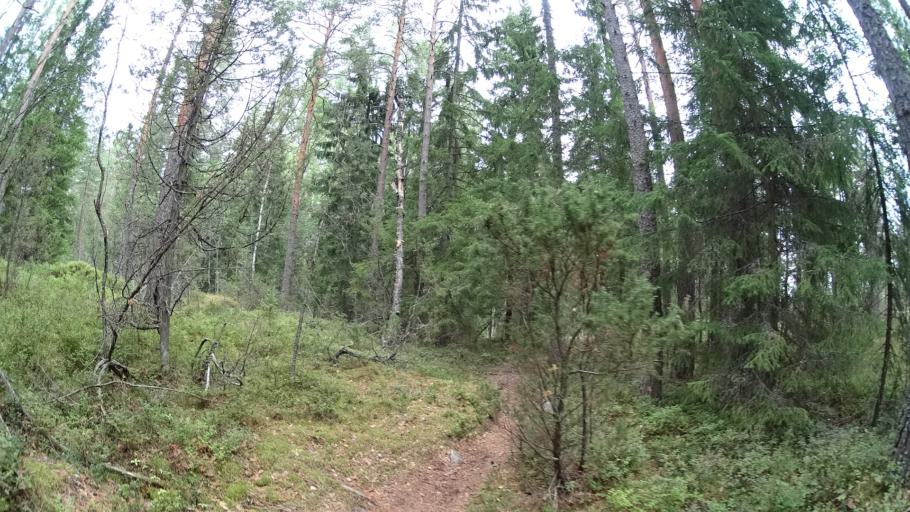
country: FI
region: Uusimaa
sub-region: Helsinki
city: Espoo
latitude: 60.3080
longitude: 24.5796
